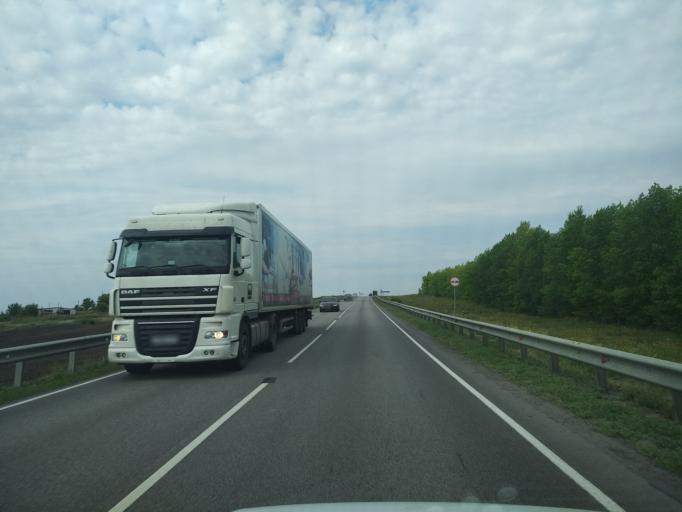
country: RU
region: Voronezj
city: Pereleshinskiy
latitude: 51.8546
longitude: 40.3340
